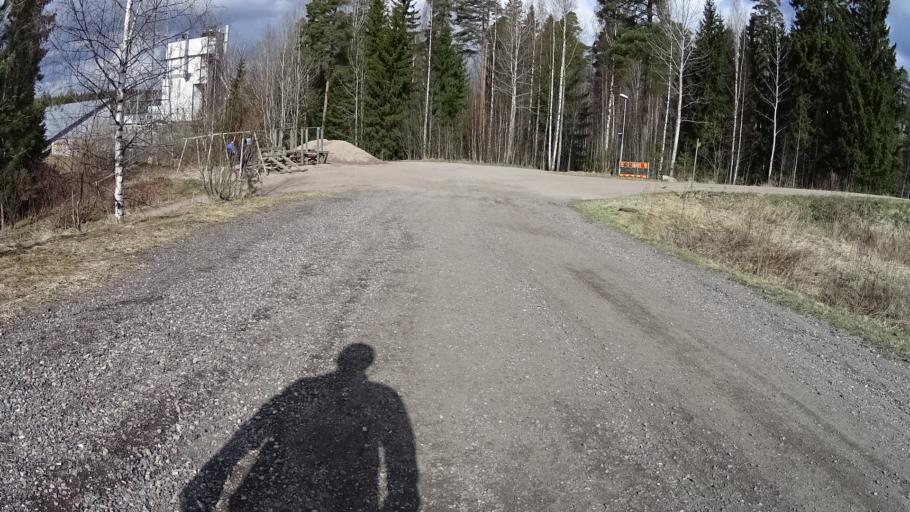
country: FI
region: Uusimaa
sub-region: Helsinki
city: Teekkarikylae
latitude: 60.2516
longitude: 24.8398
